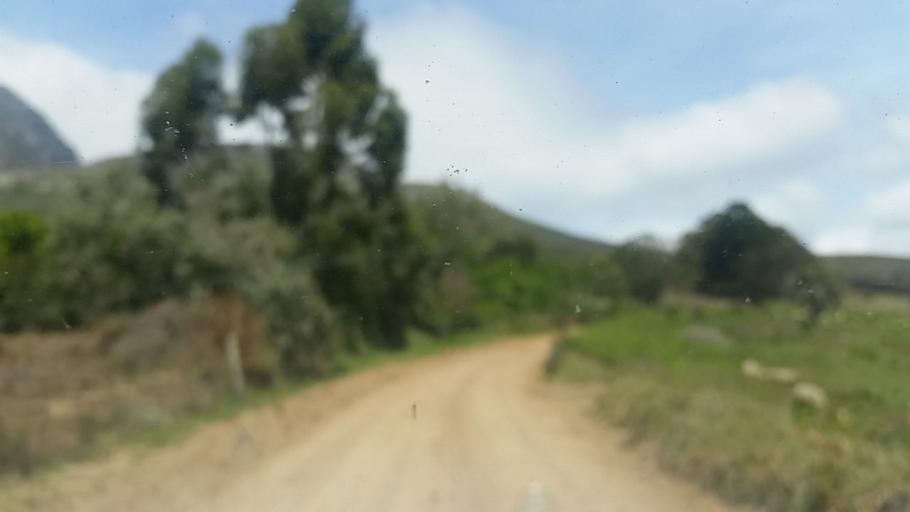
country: ZA
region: Western Cape
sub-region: Eden District Municipality
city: George
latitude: -33.8781
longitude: 22.4402
